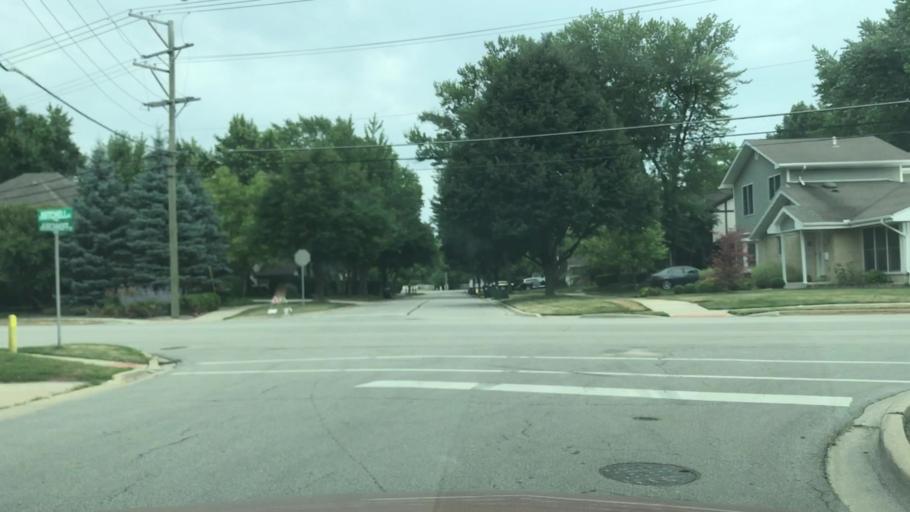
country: US
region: Illinois
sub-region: Cook County
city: Arlington Heights
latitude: 42.0687
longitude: -87.9880
